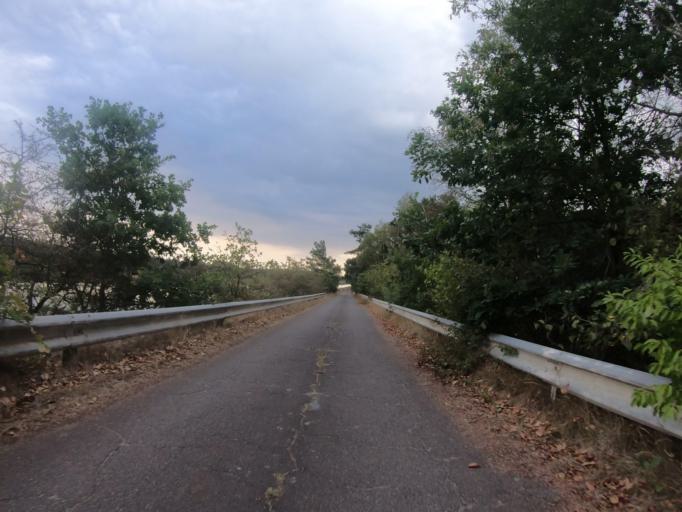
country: DE
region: Lower Saxony
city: Sassenburg
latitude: 52.5561
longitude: 10.6605
